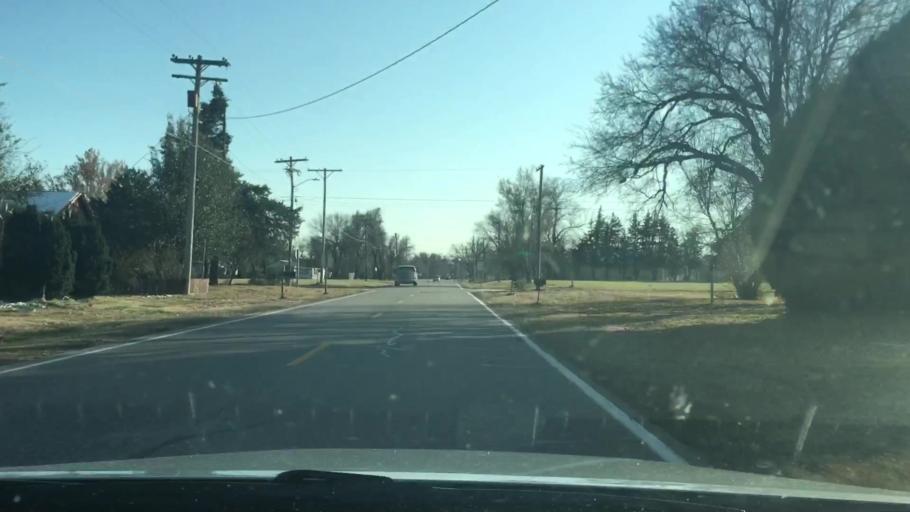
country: US
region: Kansas
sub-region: Reno County
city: Nickerson
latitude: 38.1547
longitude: -98.0874
